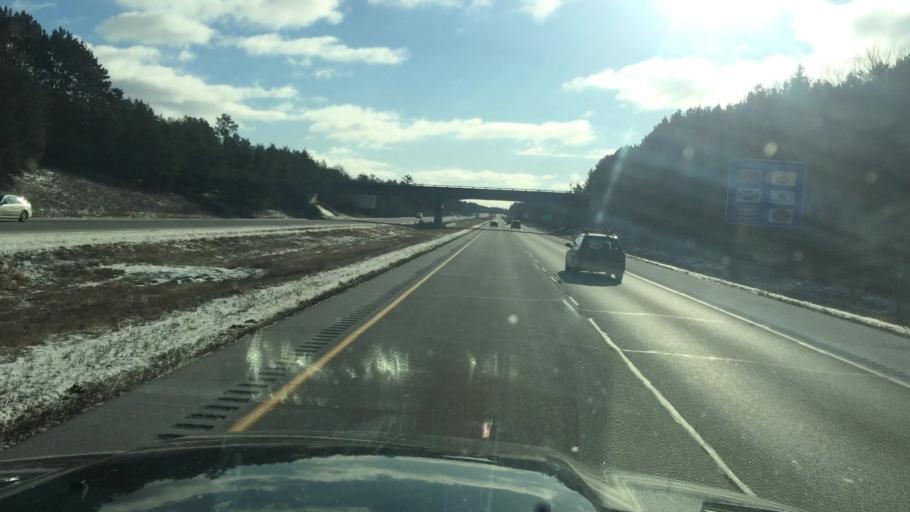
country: US
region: Wisconsin
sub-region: Portage County
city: Stevens Point
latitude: 44.5318
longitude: -89.5359
